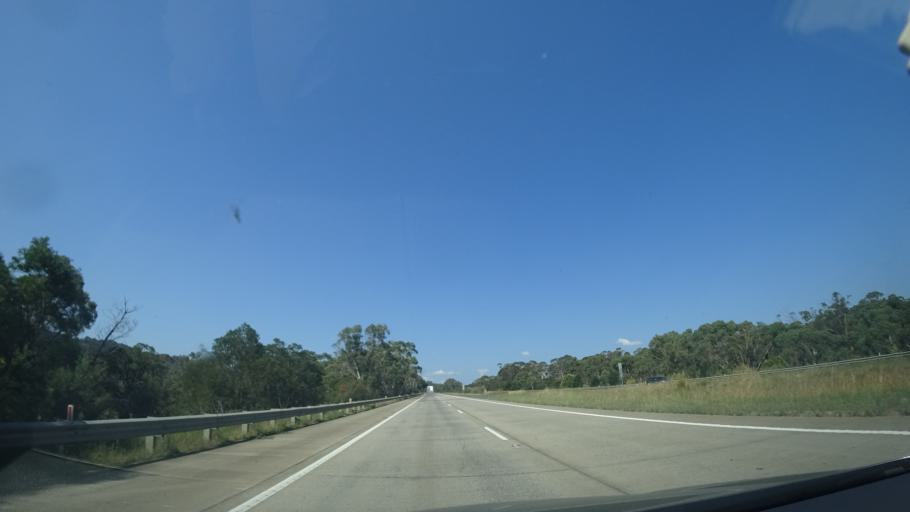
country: AU
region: New South Wales
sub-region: Wingecarribee
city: Bowral
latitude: -34.4673
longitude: 150.3407
